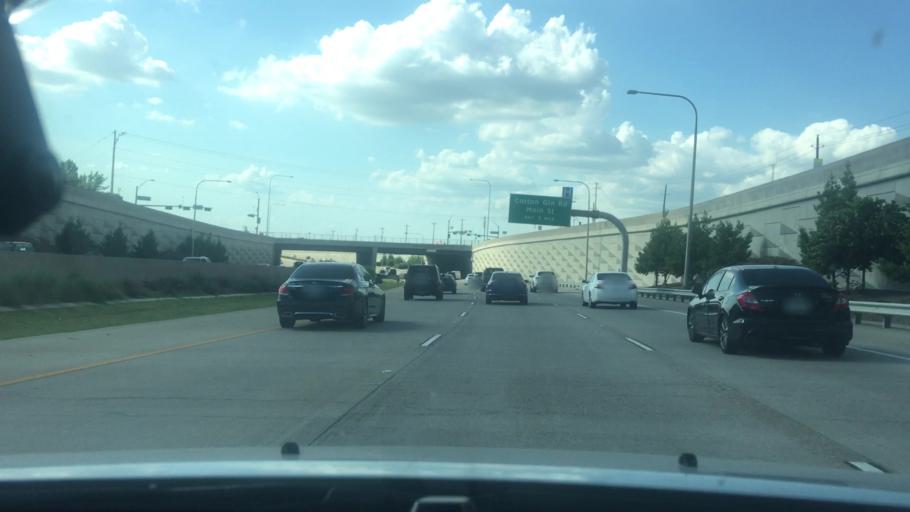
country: US
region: Texas
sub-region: Collin County
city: Frisco
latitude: 33.1299
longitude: -96.8240
